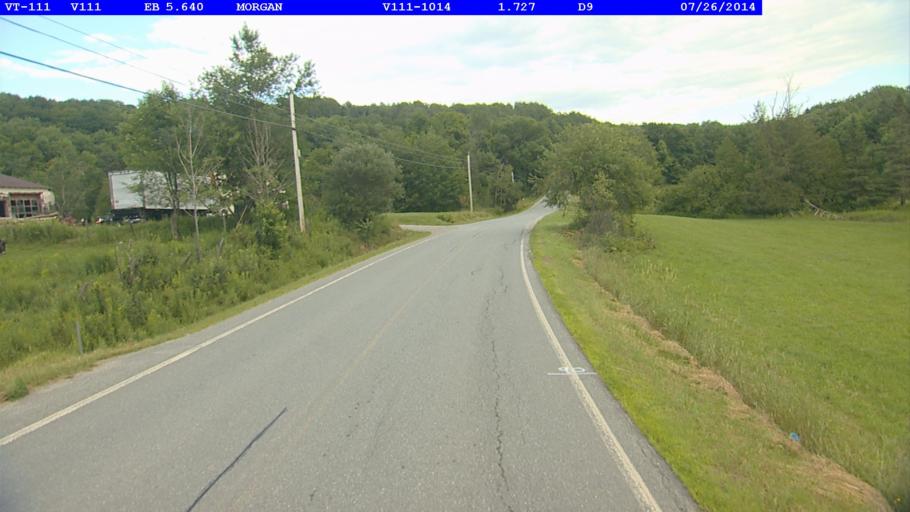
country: US
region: Vermont
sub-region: Orleans County
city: Newport
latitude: 44.9222
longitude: -72.0327
